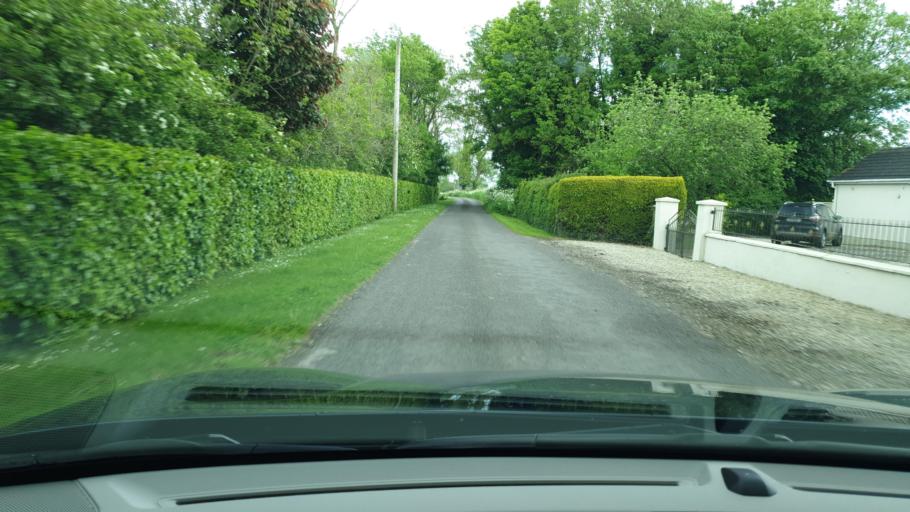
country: IE
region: Leinster
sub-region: An Mhi
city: Ratoath
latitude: 53.5278
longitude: -6.4725
